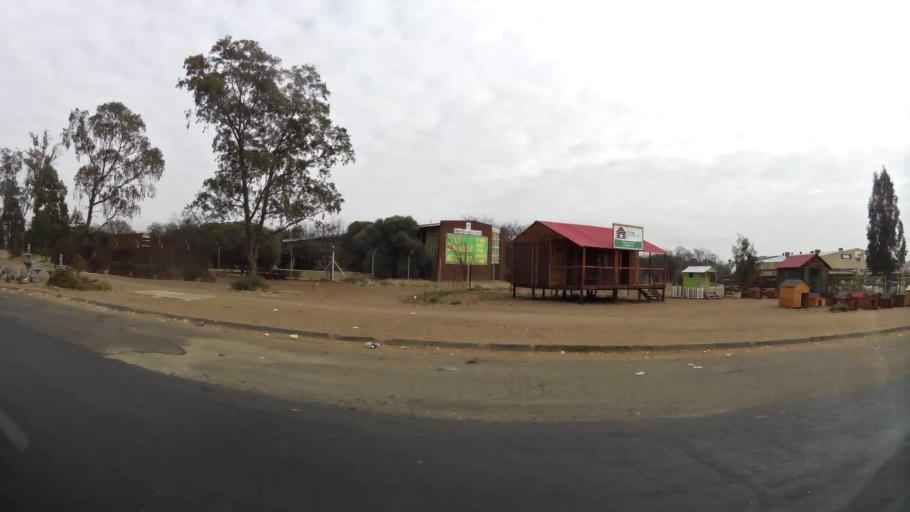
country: ZA
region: Orange Free State
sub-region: Mangaung Metropolitan Municipality
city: Bloemfontein
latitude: -29.1365
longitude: 26.2030
